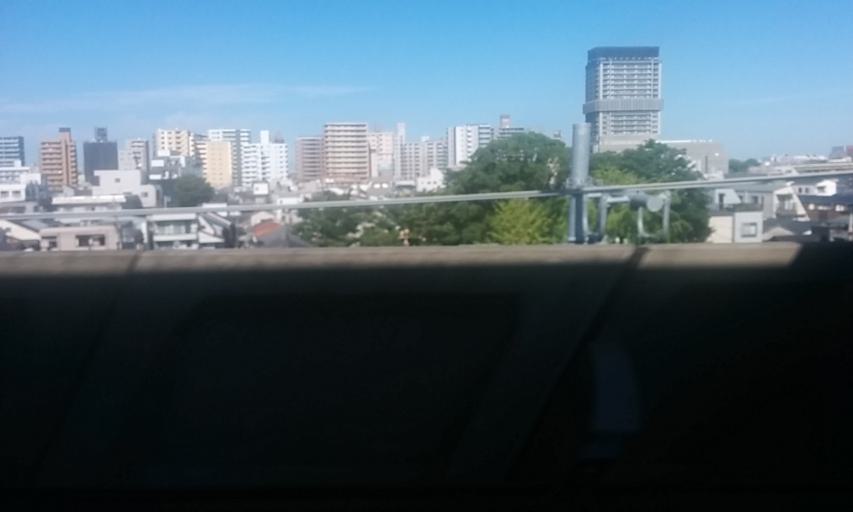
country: JP
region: Saitama
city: Soka
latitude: 35.7538
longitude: 139.8064
